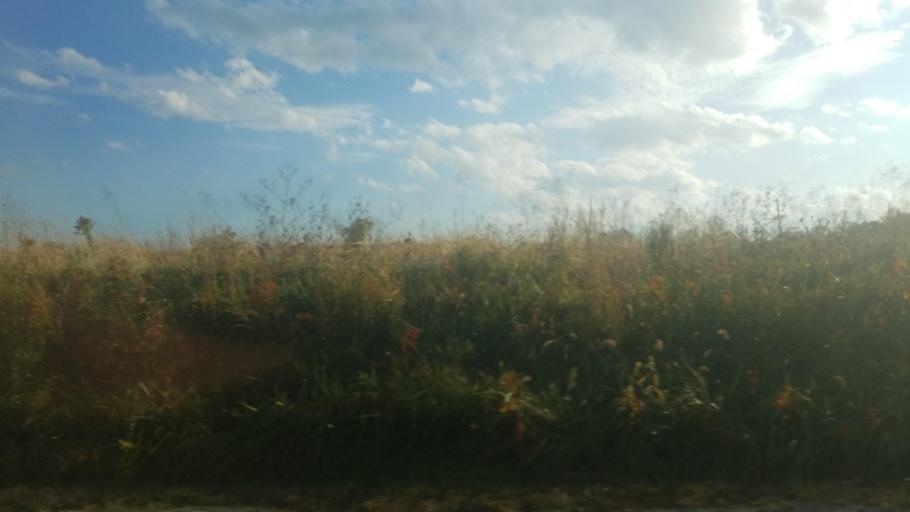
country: US
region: Illinois
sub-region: Saline County
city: Carrier Mills
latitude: 37.8050
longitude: -88.6926
